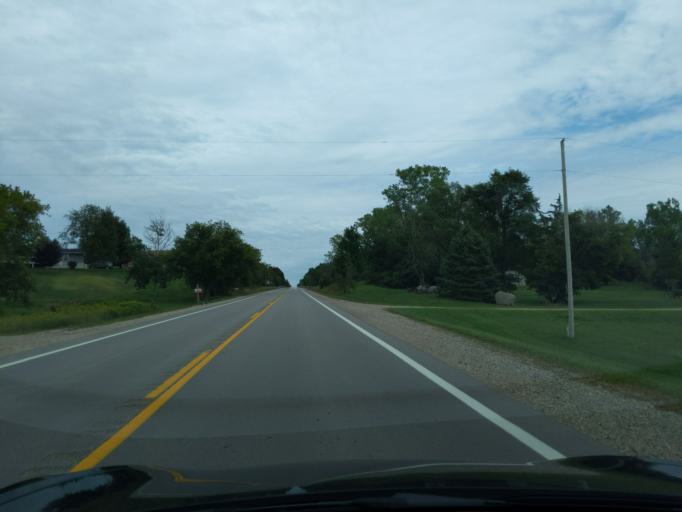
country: US
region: Michigan
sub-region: Barry County
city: Nashville
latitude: 42.5673
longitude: -85.0783
